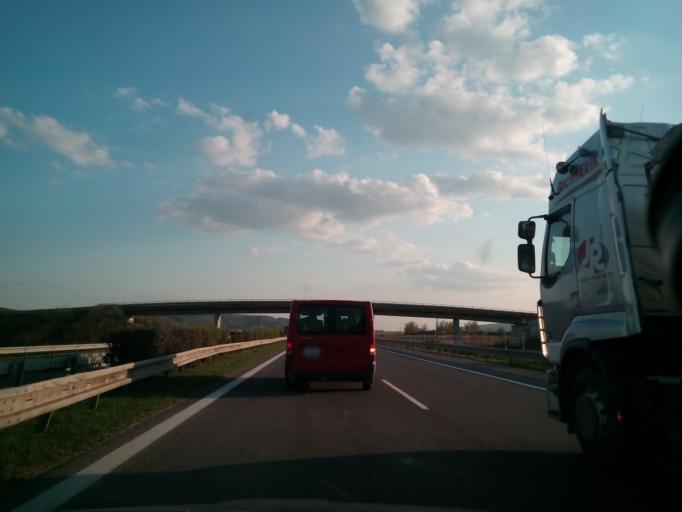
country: SK
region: Trenciansky
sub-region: Okres Trencin
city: Trencin
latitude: 48.8481
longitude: 17.9465
